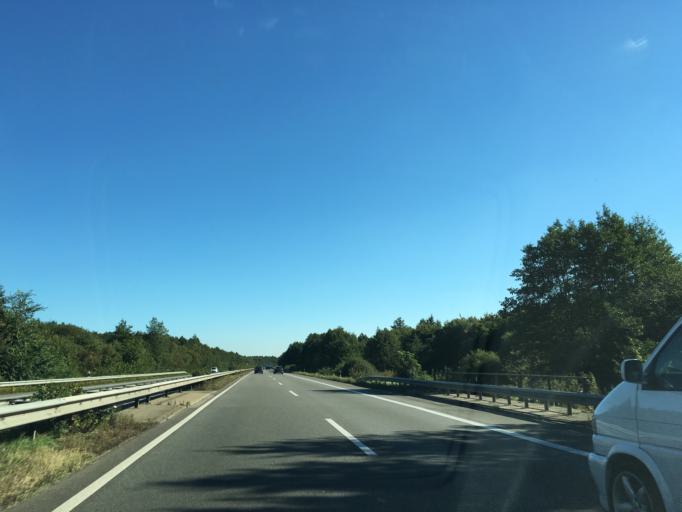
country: DE
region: Lower Saxony
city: Radbruch
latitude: 53.3300
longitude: 10.2754
